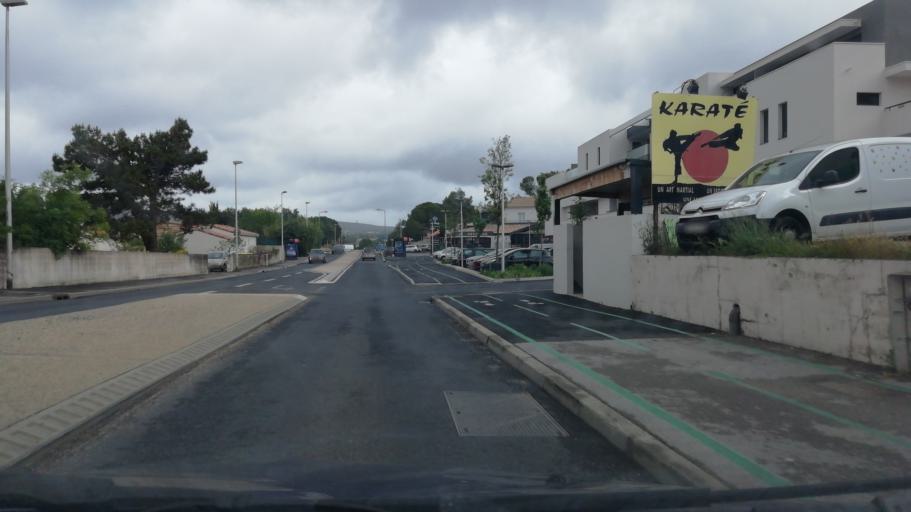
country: FR
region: Languedoc-Roussillon
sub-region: Departement de l'Herault
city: Saint-Gely-du-Fesc
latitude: 43.6807
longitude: 3.8114
